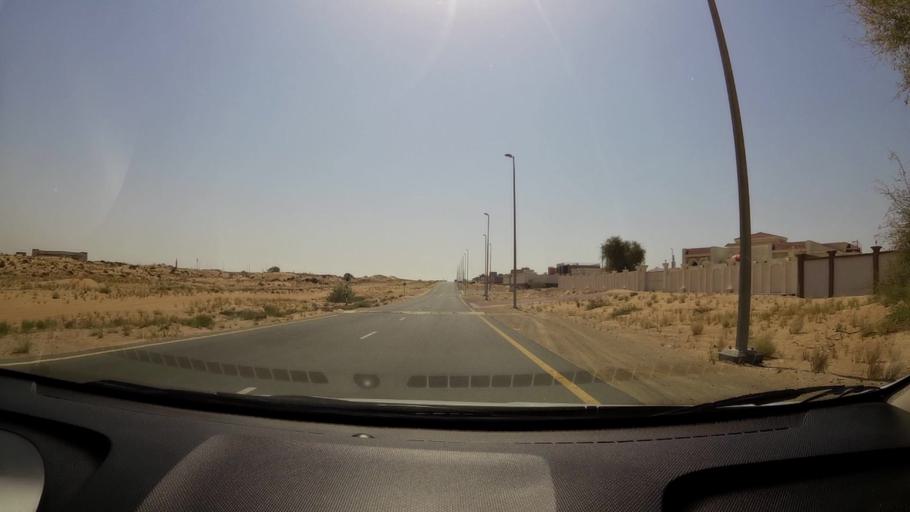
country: AE
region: Umm al Qaywayn
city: Umm al Qaywayn
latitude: 25.4808
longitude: 55.6087
